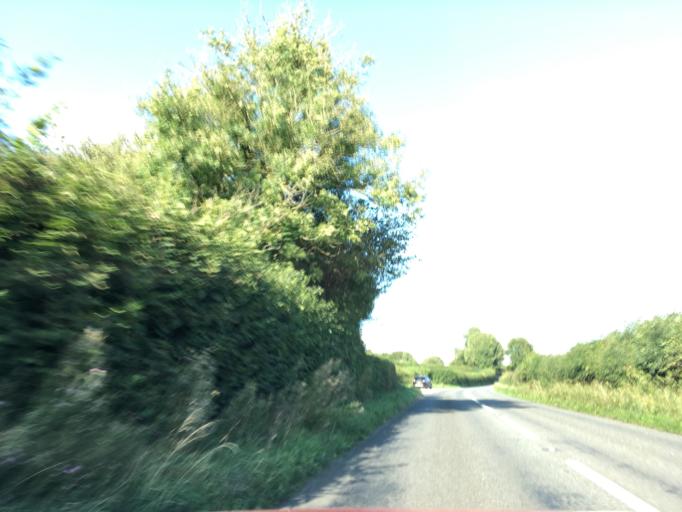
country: GB
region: England
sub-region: Somerset
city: Mendip
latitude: 51.2266
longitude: -2.6029
